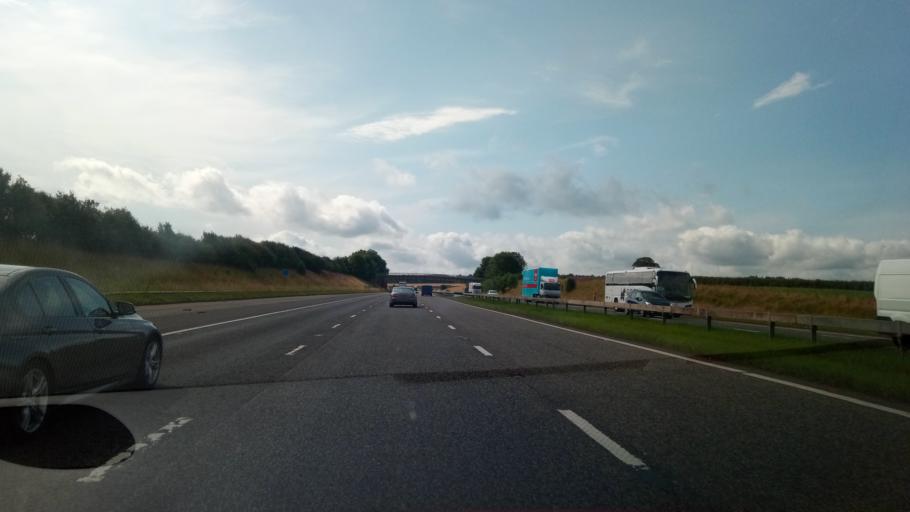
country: GB
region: England
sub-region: Cumbria
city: Penrith
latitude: 54.6257
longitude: -2.7225
